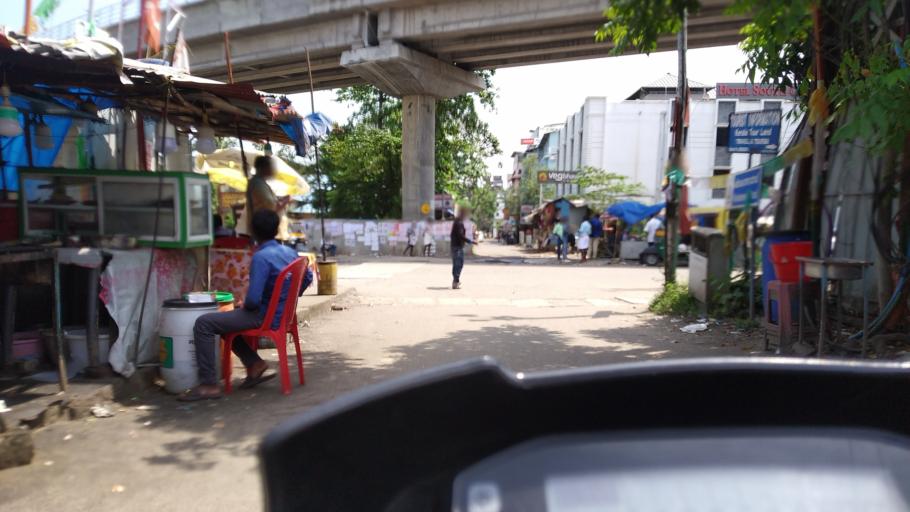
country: IN
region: Kerala
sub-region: Ernakulam
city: Cochin
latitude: 9.9689
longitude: 76.2902
